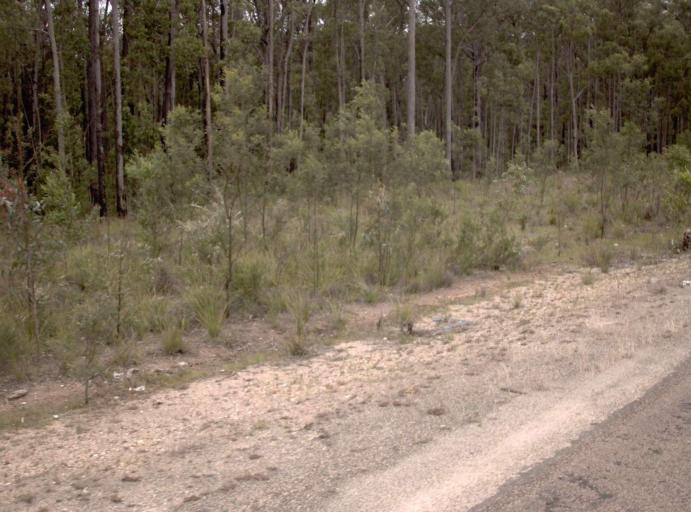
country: AU
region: Victoria
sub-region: East Gippsland
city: Lakes Entrance
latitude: -37.7044
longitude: 148.0557
